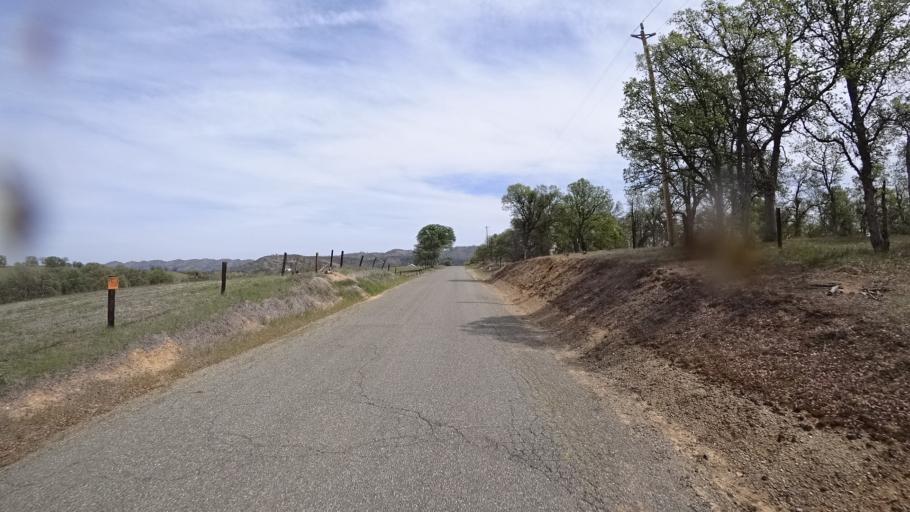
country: US
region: California
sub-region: Glenn County
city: Willows
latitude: 39.5917
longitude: -122.5592
